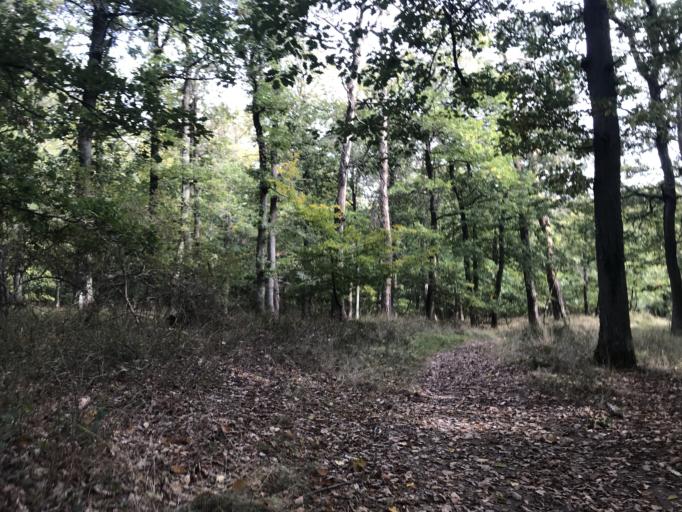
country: DE
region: Rheinland-Pfalz
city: Kirchheimbolanden
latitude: 49.6574
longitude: 7.9853
